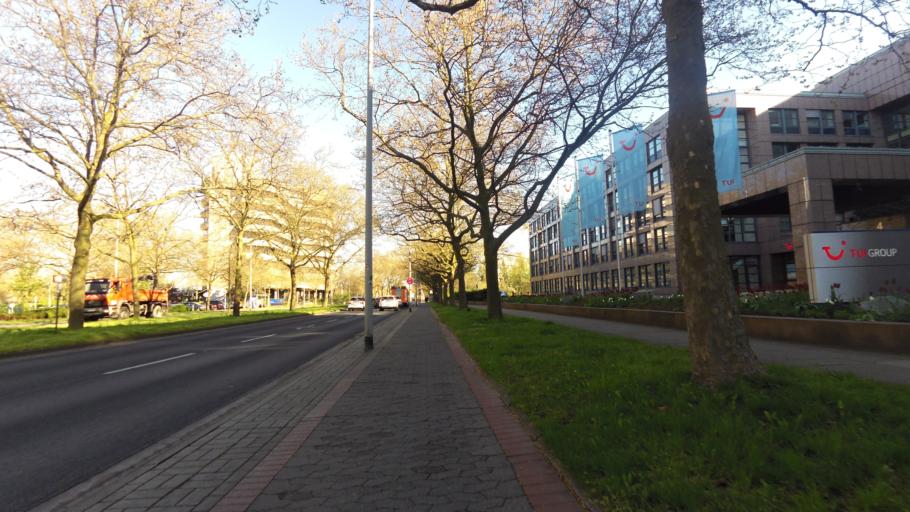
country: DE
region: Lower Saxony
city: Laatzen
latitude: 52.3835
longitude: 9.8106
